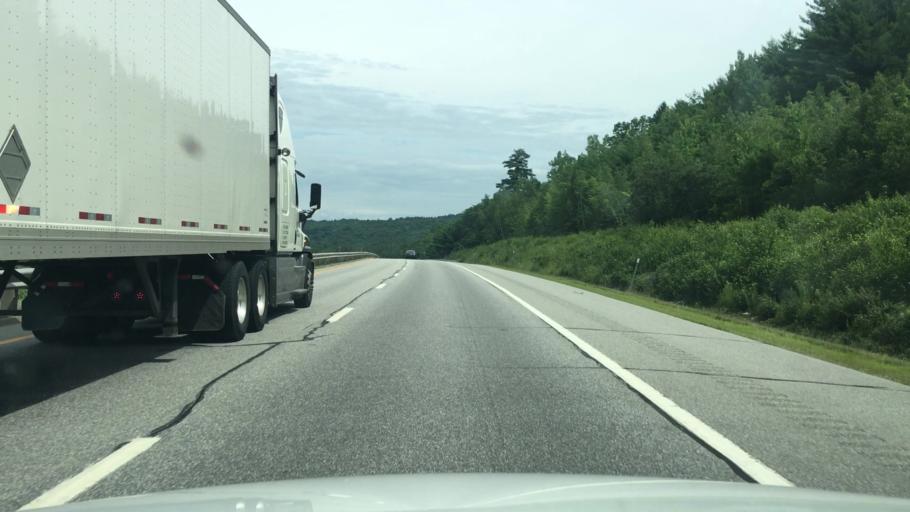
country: US
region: New Hampshire
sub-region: Grafton County
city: Ashland
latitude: 43.6376
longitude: -71.6495
